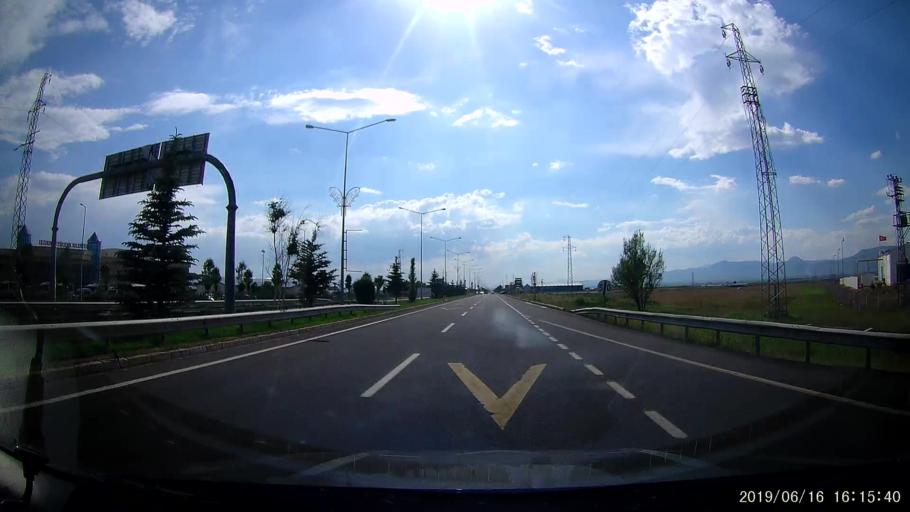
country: TR
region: Erzurum
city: Erzurum
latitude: 39.9621
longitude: 41.2213
